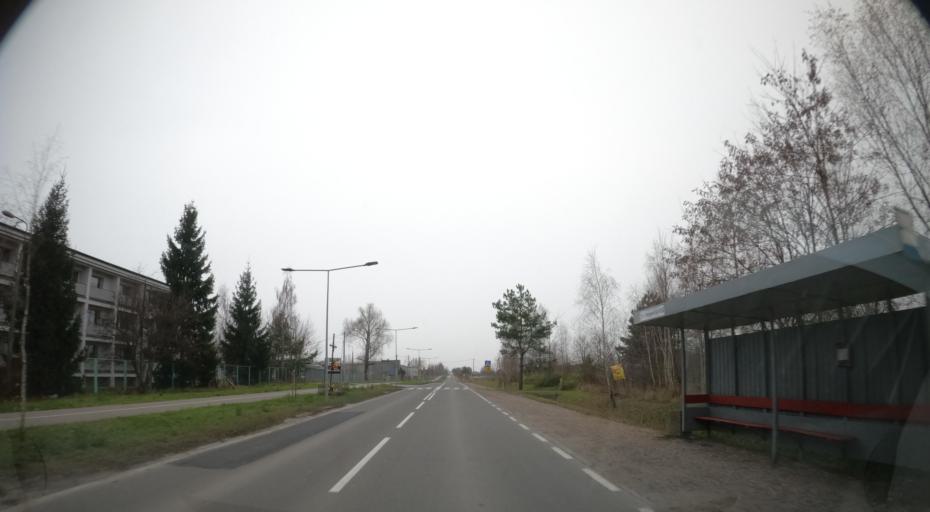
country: PL
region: Masovian Voivodeship
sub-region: Radom
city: Radom
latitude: 51.4451
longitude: 21.1913
